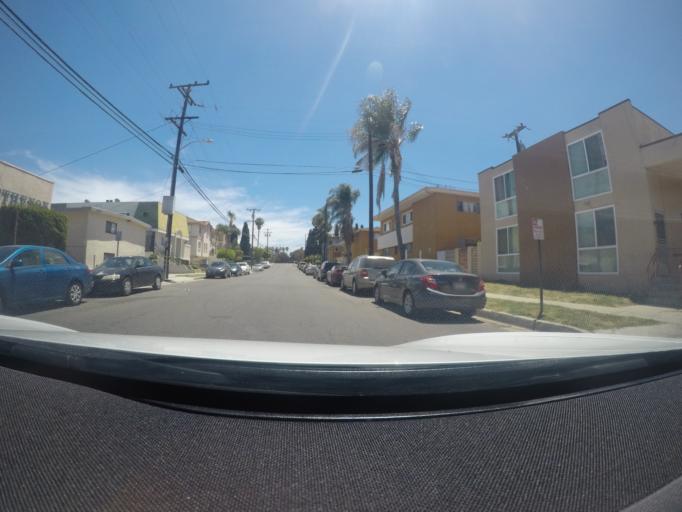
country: US
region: California
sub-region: Los Angeles County
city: Torrance
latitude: 33.8408
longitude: -118.3506
